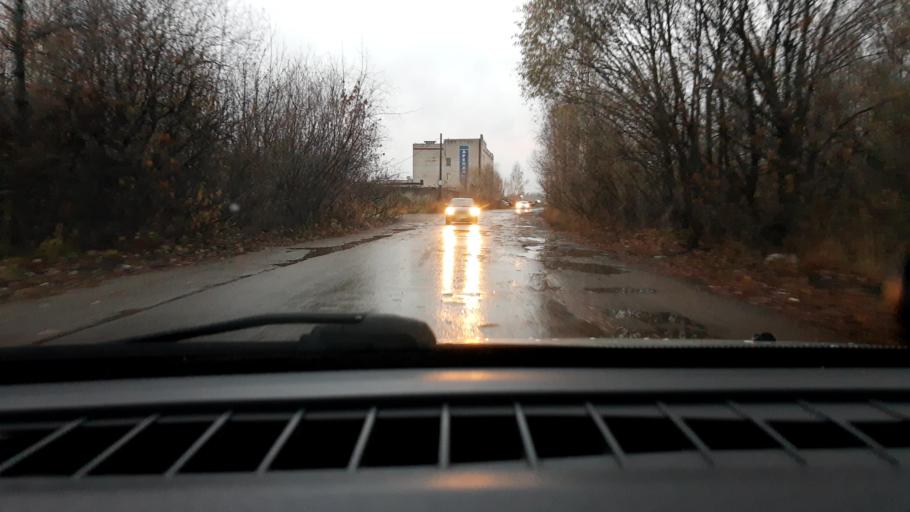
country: RU
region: Nizjnij Novgorod
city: Gorbatovka
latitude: 56.2692
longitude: 43.8554
